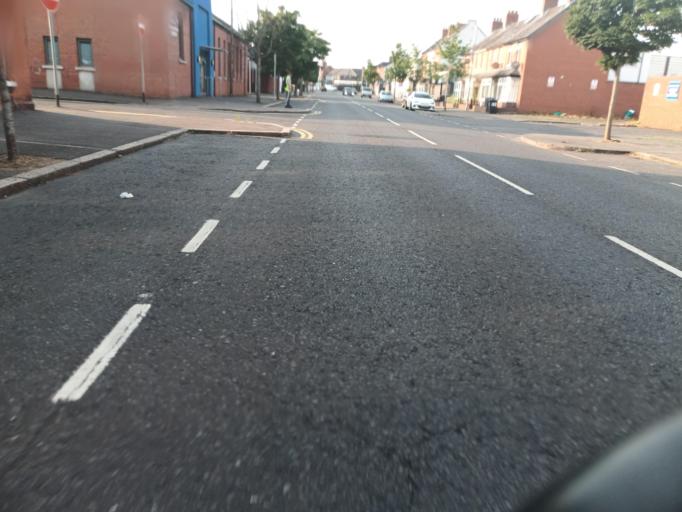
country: GB
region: Northern Ireland
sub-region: Castlereagh District
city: Castlereagh
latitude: 54.5953
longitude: -5.8880
